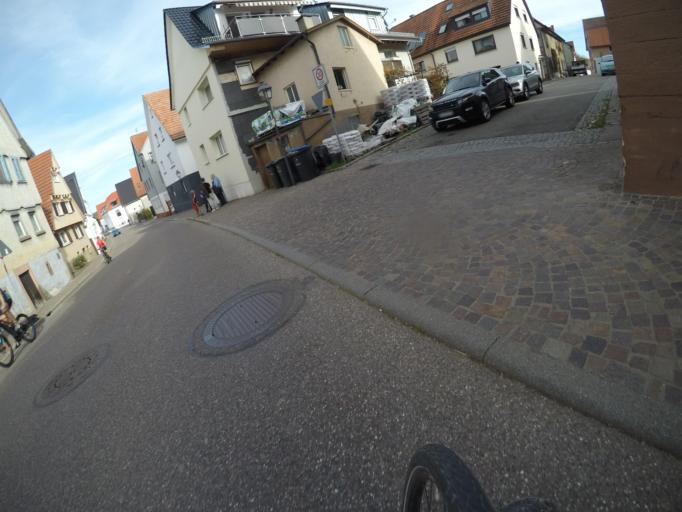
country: DE
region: Baden-Wuerttemberg
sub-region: Regierungsbezirk Stuttgart
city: Weil der Stadt
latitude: 48.7695
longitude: 8.8526
